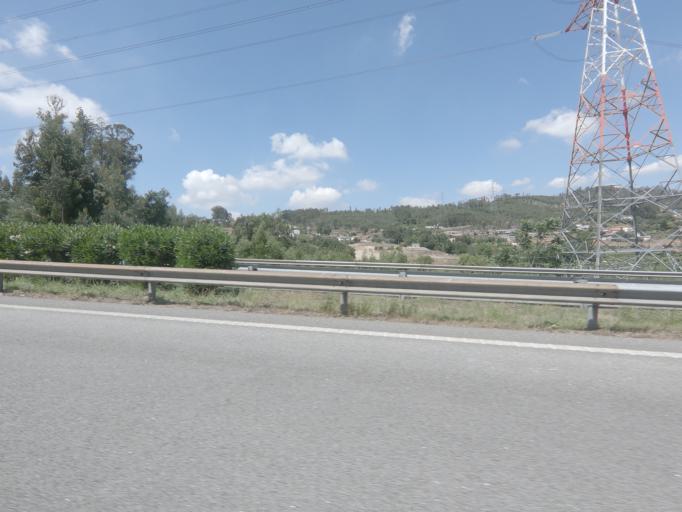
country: PT
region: Porto
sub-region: Paredes
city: Baltar
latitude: 41.1921
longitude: -8.3588
